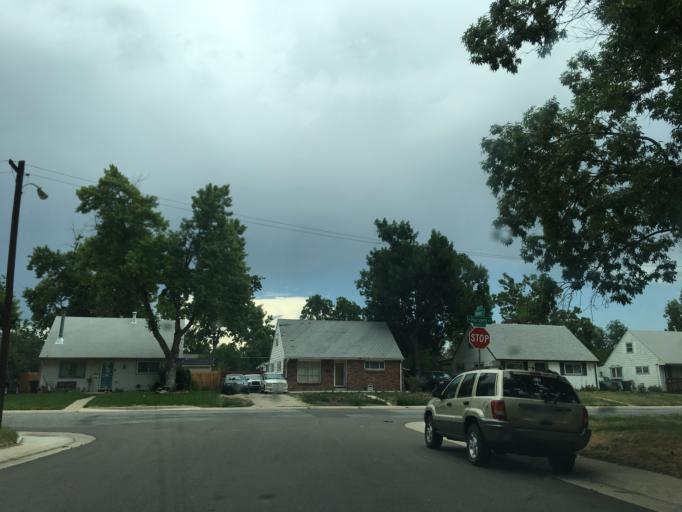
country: US
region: Colorado
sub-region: Arapahoe County
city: Sheridan
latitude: 39.6728
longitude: -105.0290
